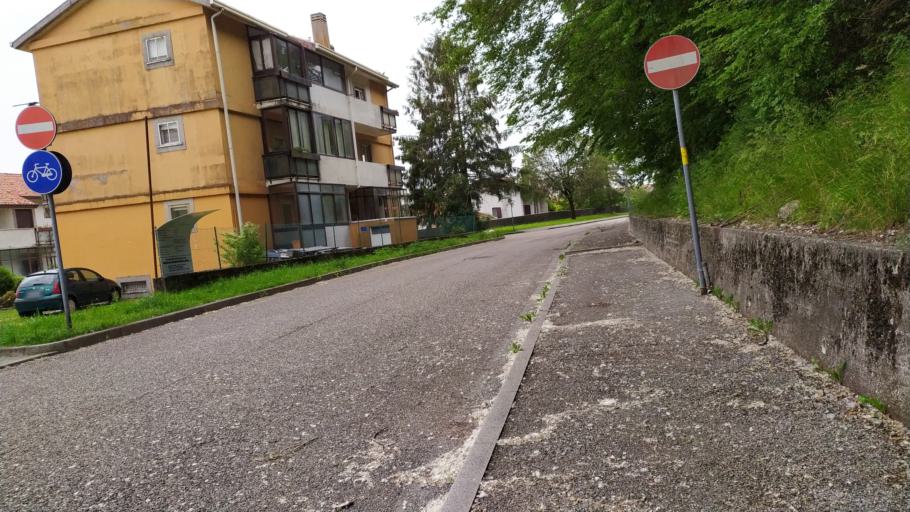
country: IT
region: Friuli Venezia Giulia
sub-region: Provincia di Udine
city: Osoppo
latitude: 46.2584
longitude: 13.0828
